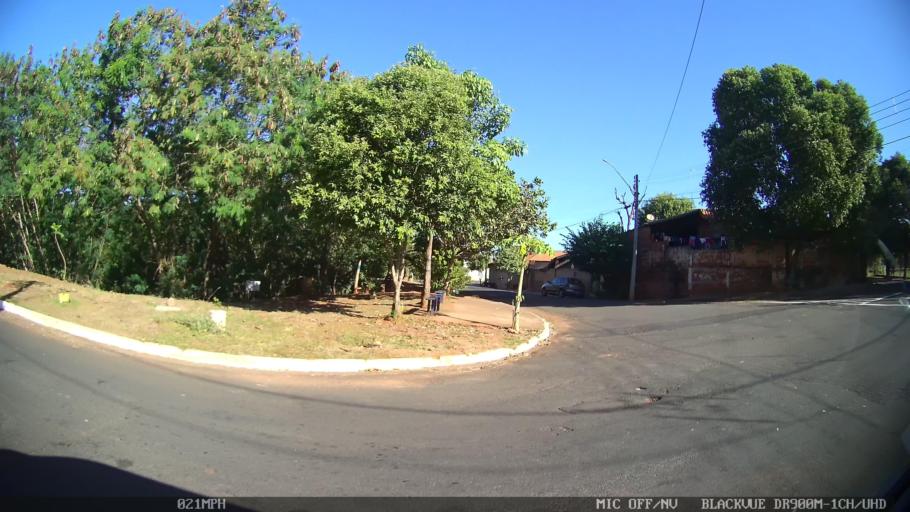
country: BR
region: Sao Paulo
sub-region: Olimpia
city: Olimpia
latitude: -20.7408
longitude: -48.8853
